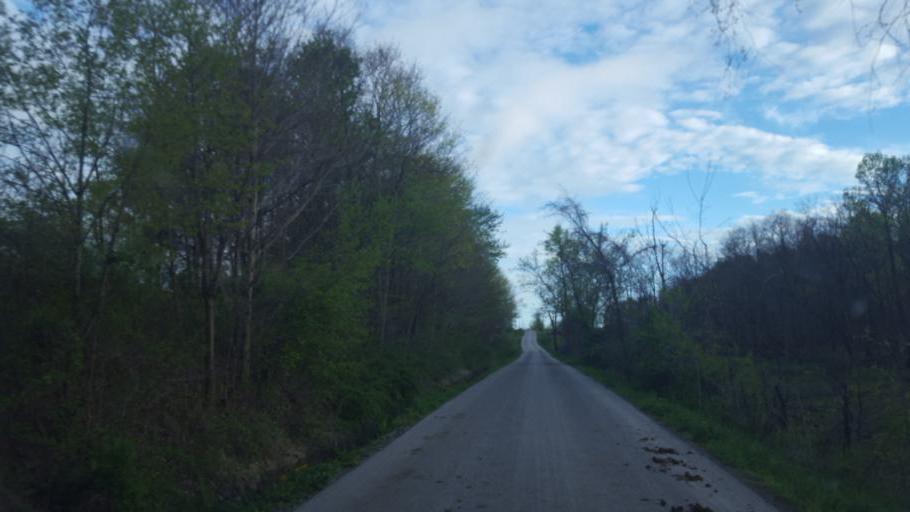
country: US
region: Ohio
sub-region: Knox County
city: Fredericktown
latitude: 40.5014
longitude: -82.6057
